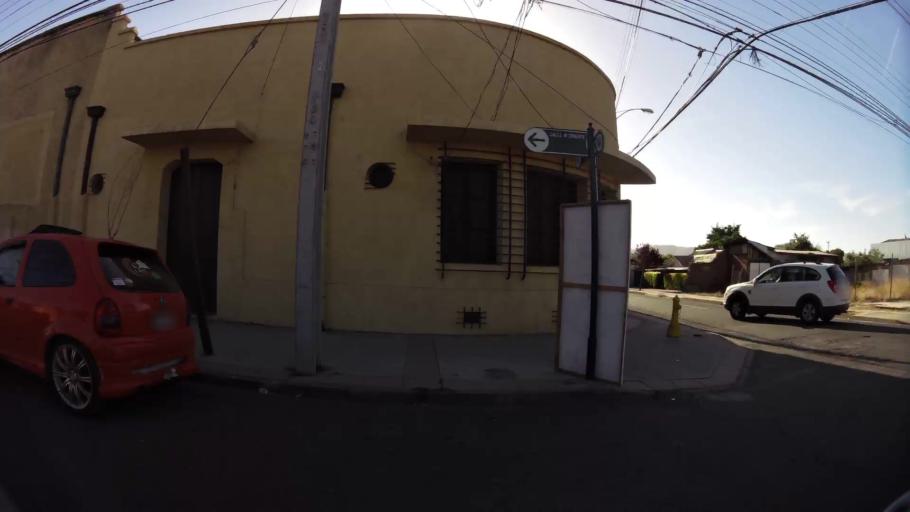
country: CL
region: Maule
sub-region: Provincia de Talca
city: Talca
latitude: -35.4329
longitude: -71.6543
